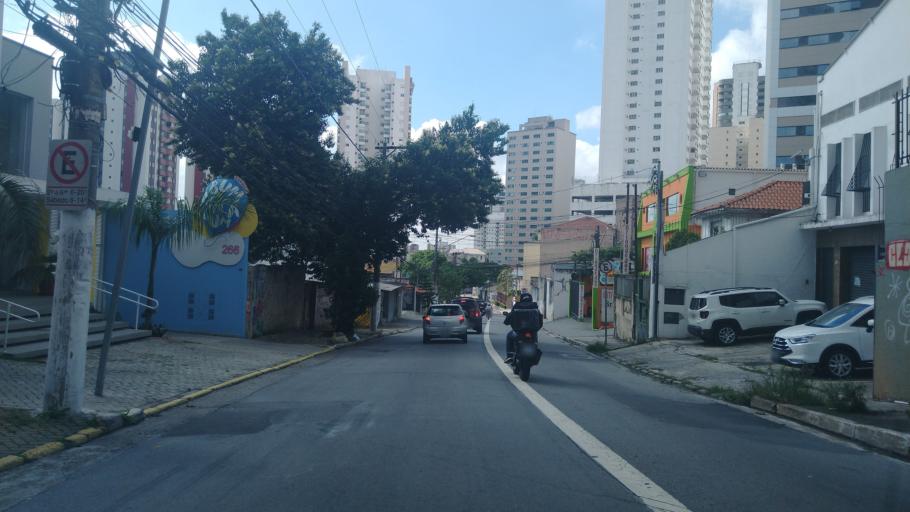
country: BR
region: Sao Paulo
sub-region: Sao Paulo
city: Sao Paulo
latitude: -23.4946
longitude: -46.6246
